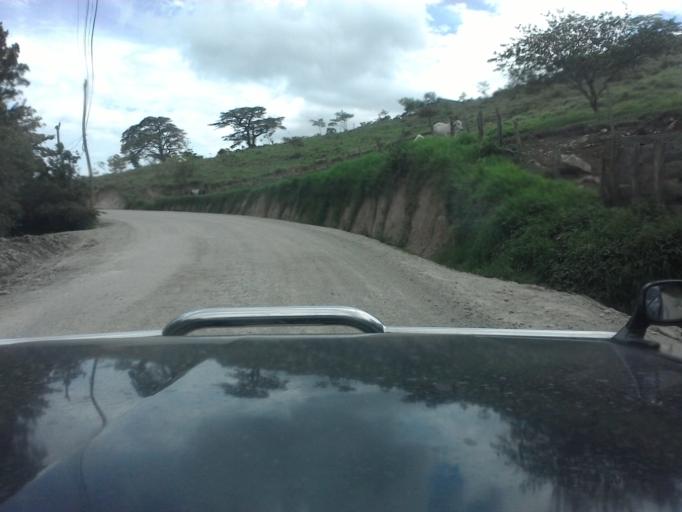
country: CR
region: Guanacaste
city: Juntas
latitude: 10.2771
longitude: -84.8415
